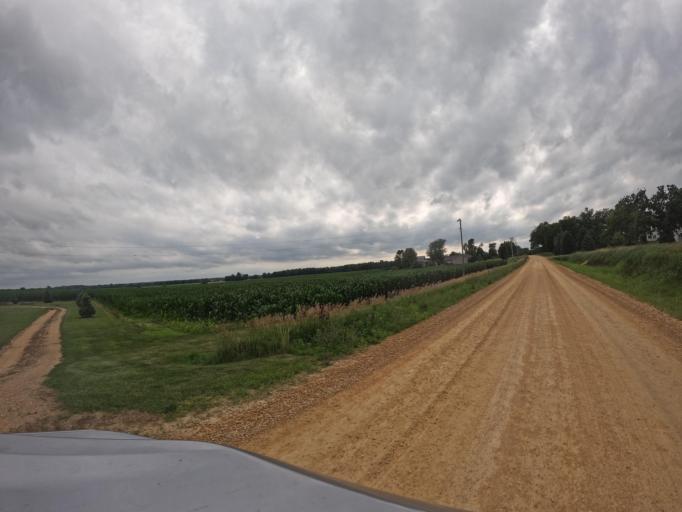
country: US
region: Iowa
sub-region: Clinton County
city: De Witt
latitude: 41.7989
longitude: -90.5495
